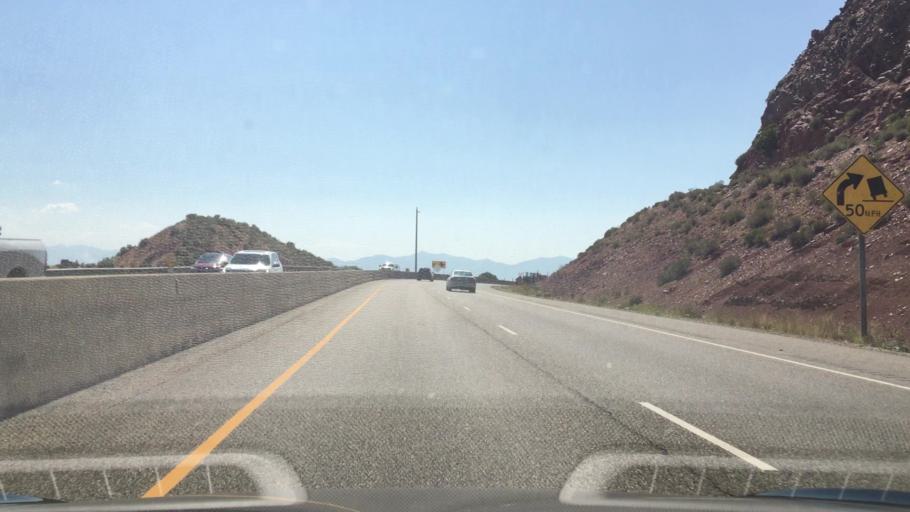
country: US
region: Utah
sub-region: Salt Lake County
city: East Millcreek
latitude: 40.7116
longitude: -111.7954
